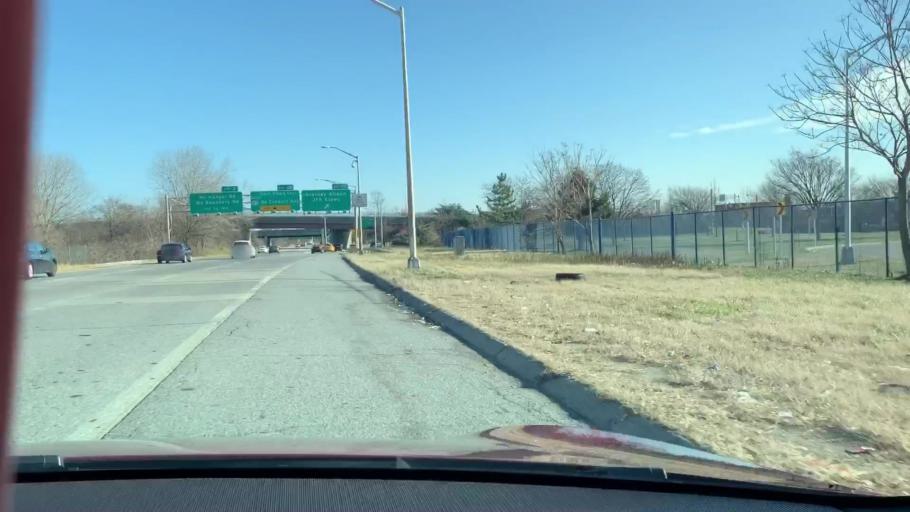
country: US
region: New York
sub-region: Queens County
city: Jamaica
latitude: 40.6647
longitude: -73.7937
